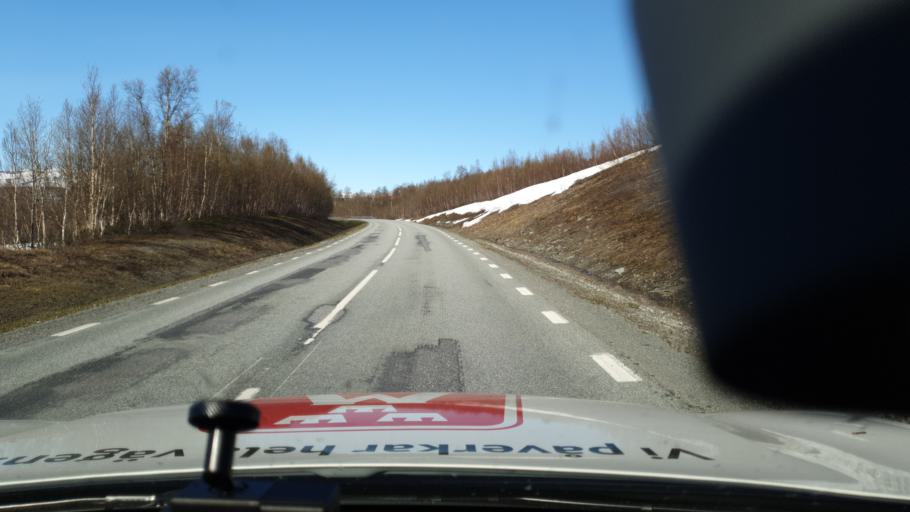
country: NO
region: Nordland
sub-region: Rana
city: Mo i Rana
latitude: 66.0001
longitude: 15.0881
